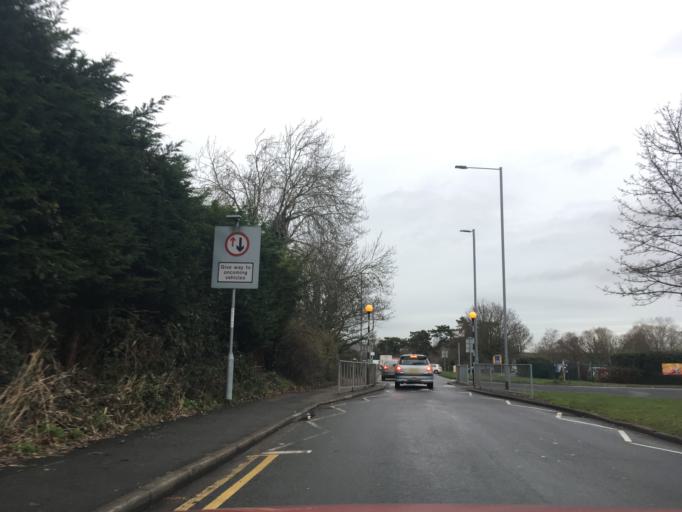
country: GB
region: Wales
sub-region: Newport
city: Nash
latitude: 51.5730
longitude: -2.9543
